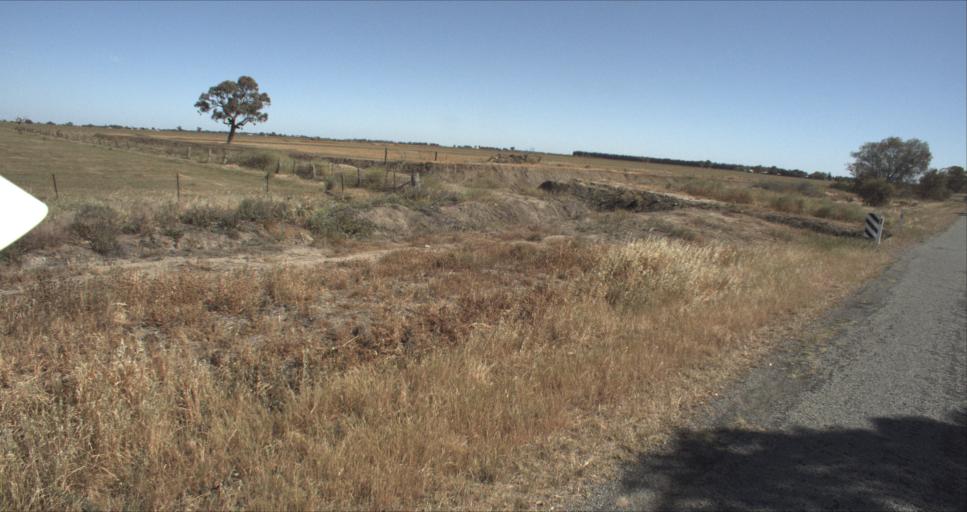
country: AU
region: New South Wales
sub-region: Leeton
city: Leeton
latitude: -34.5409
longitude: 146.3165
